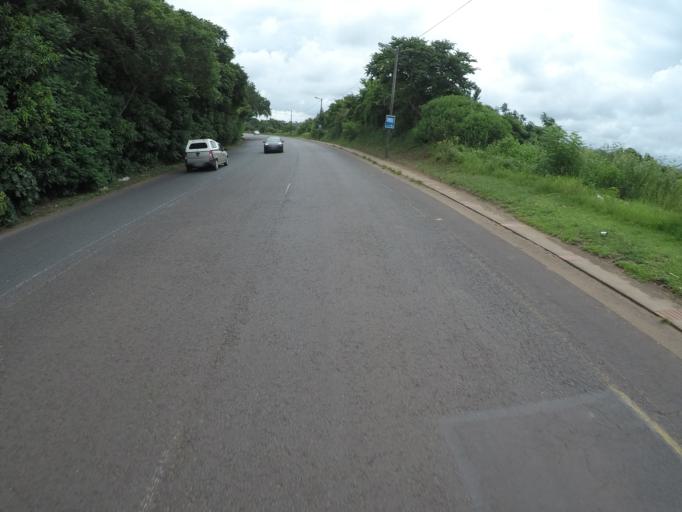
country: ZA
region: KwaZulu-Natal
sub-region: uThungulu District Municipality
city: Empangeni
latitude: -28.7757
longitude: 31.8879
